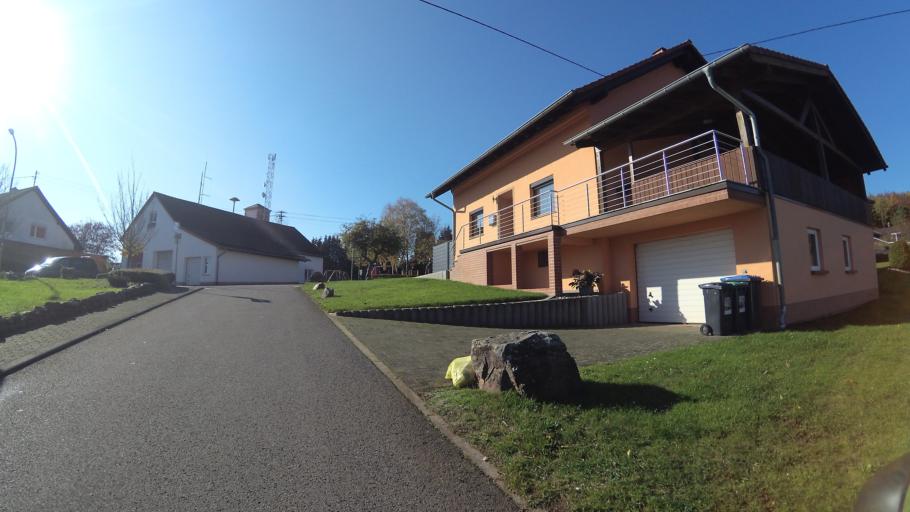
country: DE
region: Saarland
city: Losheim
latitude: 49.5474
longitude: 6.7298
